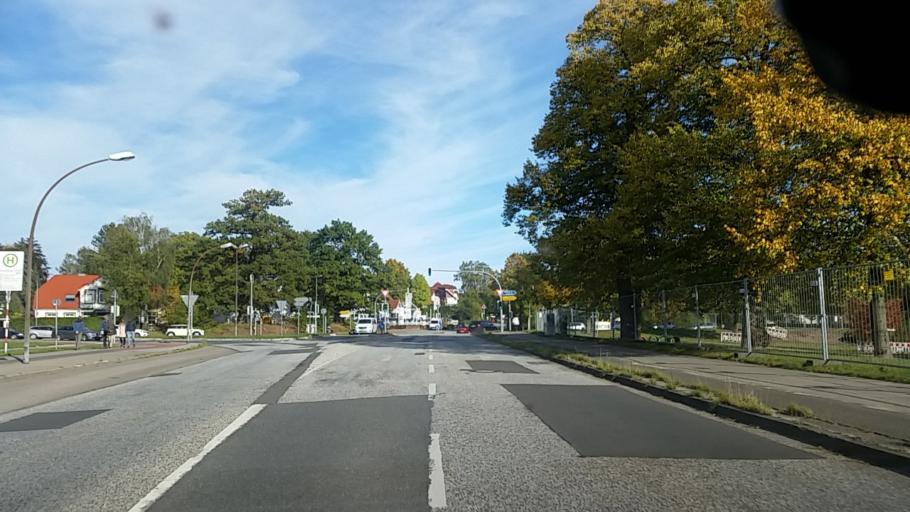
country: DE
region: Schleswig-Holstein
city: Ahrensburg
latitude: 53.6789
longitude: 10.2423
